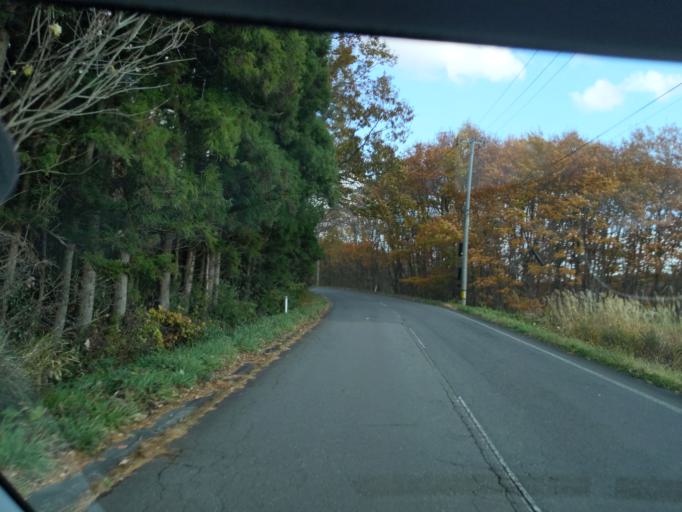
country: JP
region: Iwate
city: Mizusawa
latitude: 39.0969
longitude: 141.0055
